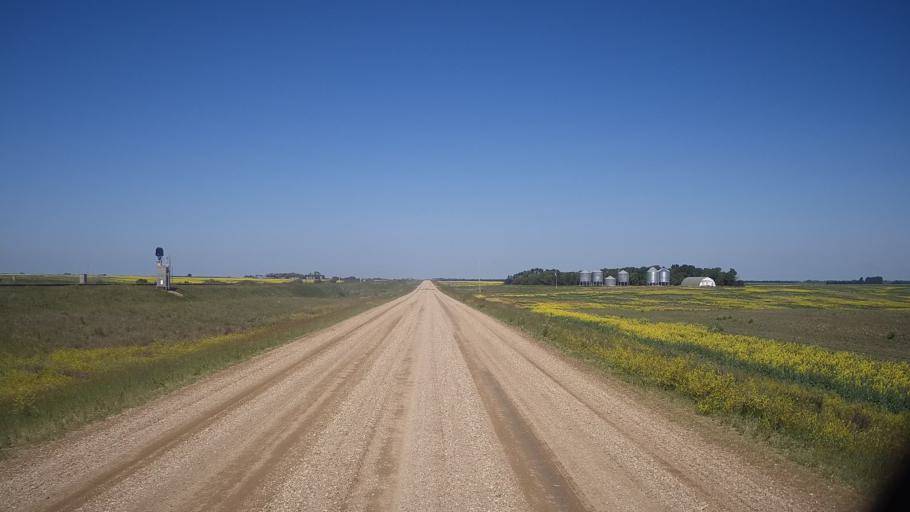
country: CA
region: Saskatchewan
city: Watrous
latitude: 51.8616
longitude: -105.9664
